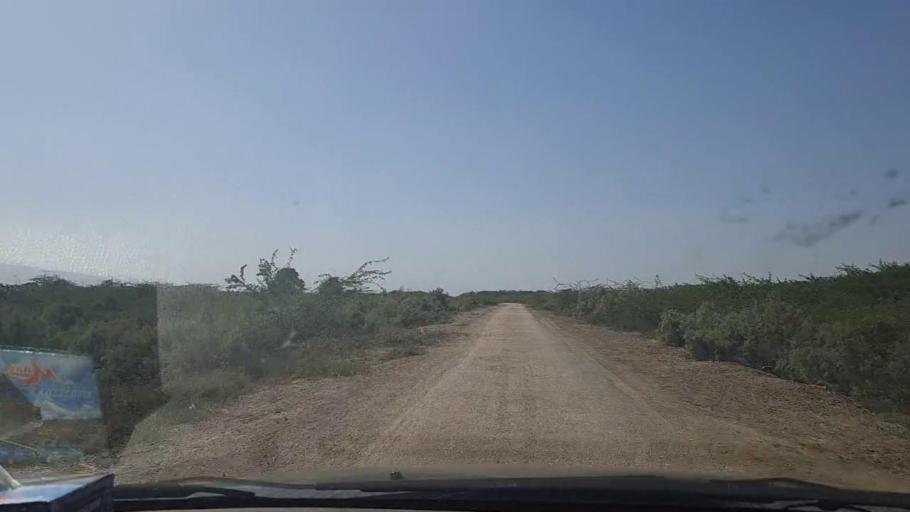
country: PK
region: Sindh
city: Chuhar Jamali
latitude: 24.2947
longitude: 67.7605
